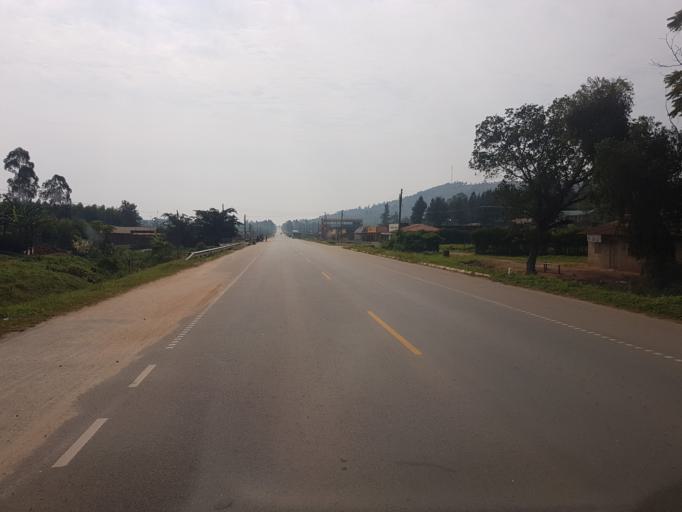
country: UG
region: Western Region
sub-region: Sheema District
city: Kibingo
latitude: -0.6429
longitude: 30.5010
